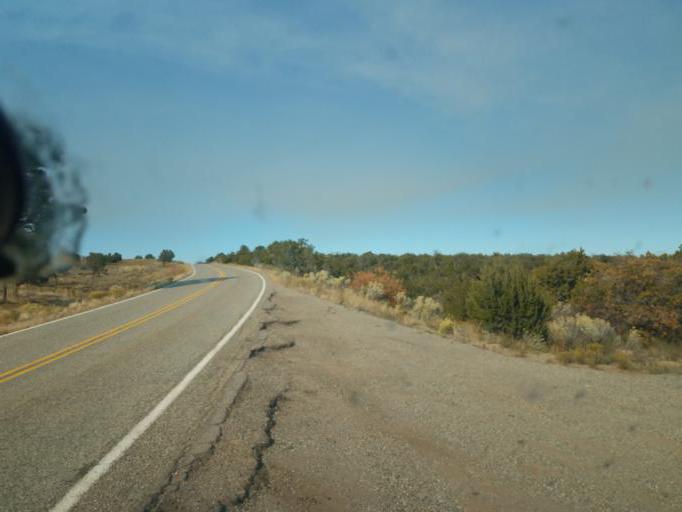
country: US
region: New Mexico
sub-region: Los Alamos County
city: White Rock
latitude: 35.7960
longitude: -106.2480
